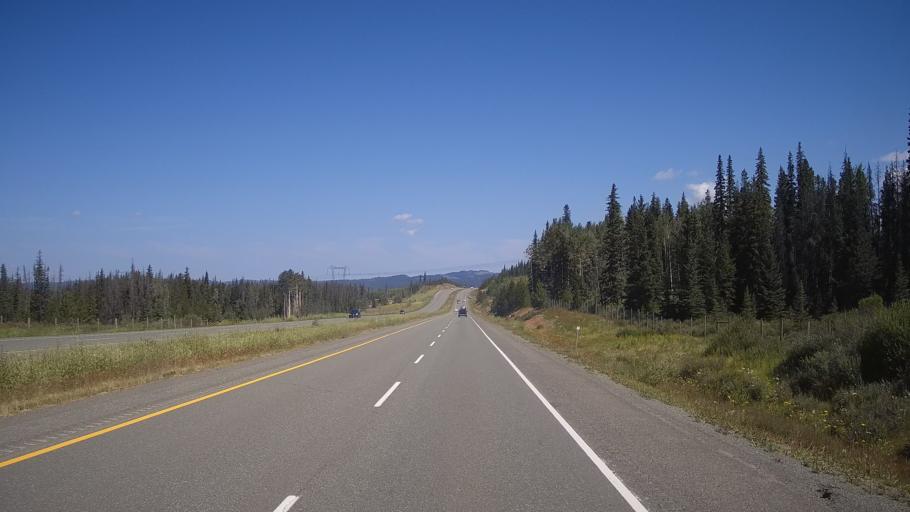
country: CA
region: British Columbia
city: Logan Lake
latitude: 50.4028
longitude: -120.6232
